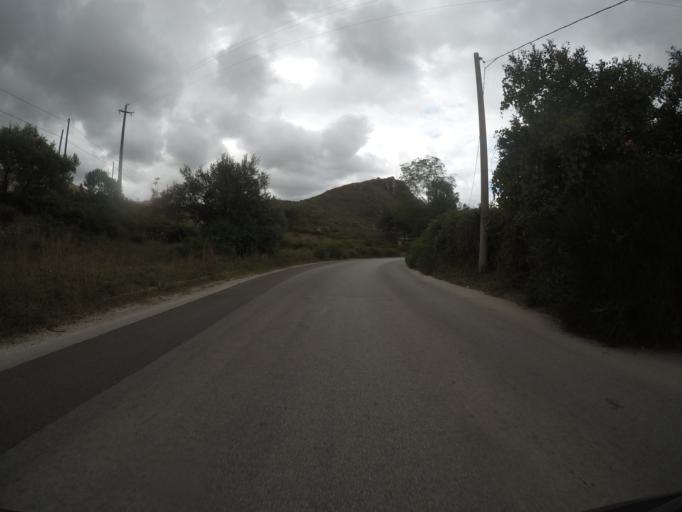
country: IT
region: Sicily
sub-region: Palermo
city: Montelepre
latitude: 38.1020
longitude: 13.1712
